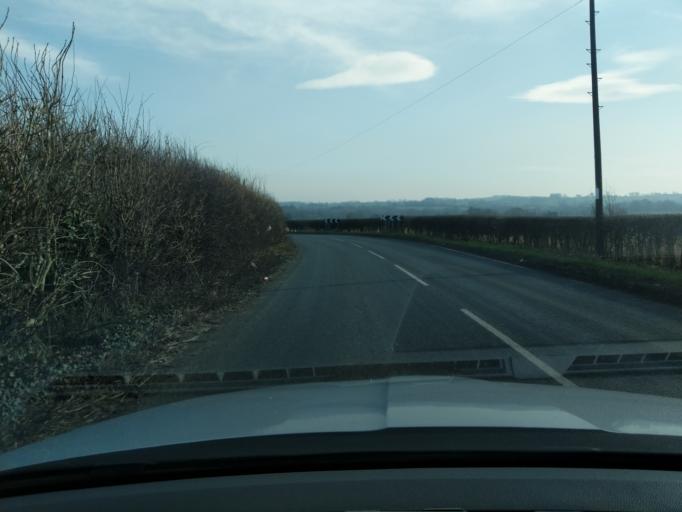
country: GB
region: England
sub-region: North Yorkshire
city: Catterick
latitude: 54.3130
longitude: -1.6726
